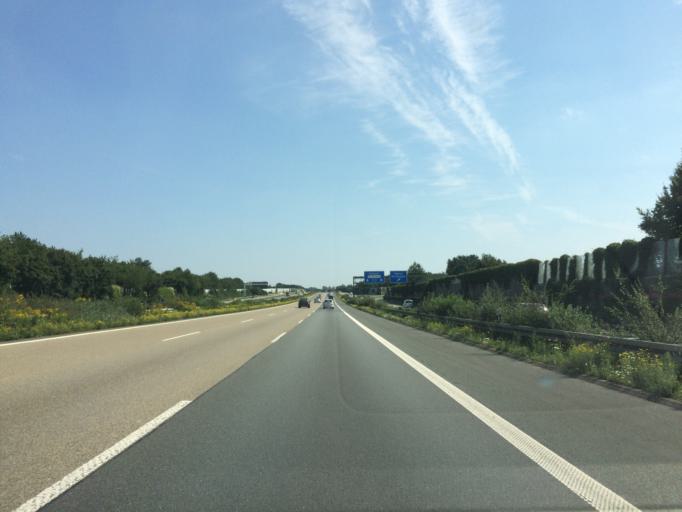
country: DE
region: North Rhine-Westphalia
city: Waltrop
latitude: 51.5844
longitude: 7.3840
